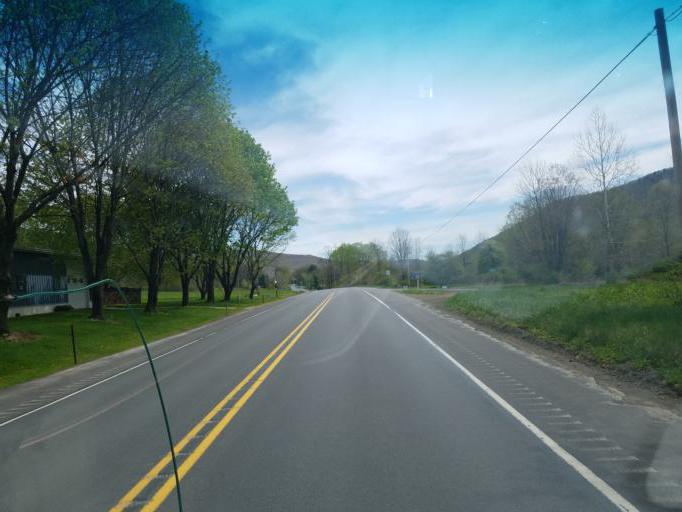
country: US
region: Pennsylvania
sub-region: Potter County
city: Galeton
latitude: 41.7473
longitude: -77.5824
